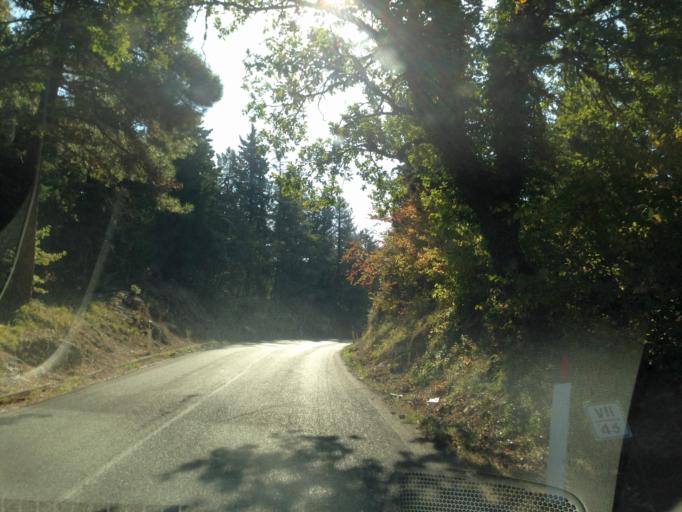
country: IT
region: Tuscany
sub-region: Provincia di Siena
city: Castellina in Chianti
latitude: 43.4519
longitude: 11.2922
